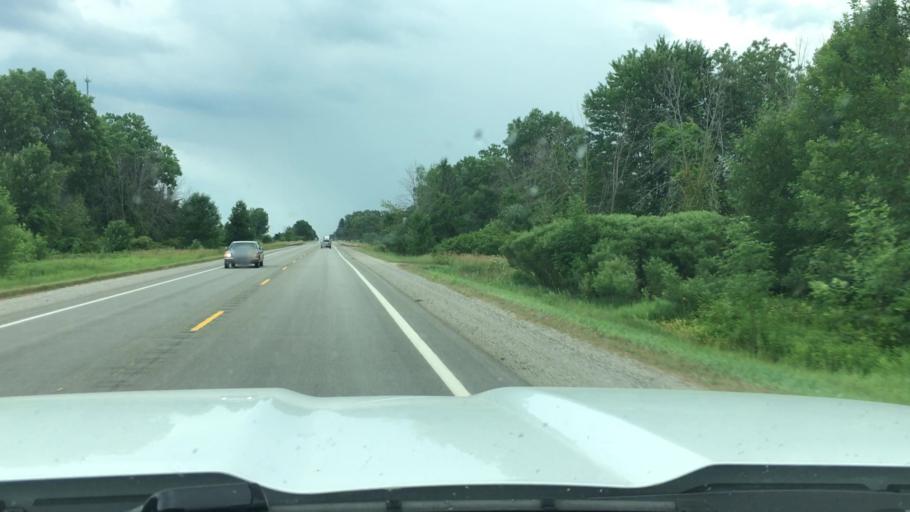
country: US
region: Michigan
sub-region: Montcalm County
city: Carson City
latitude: 43.1766
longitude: -84.8111
